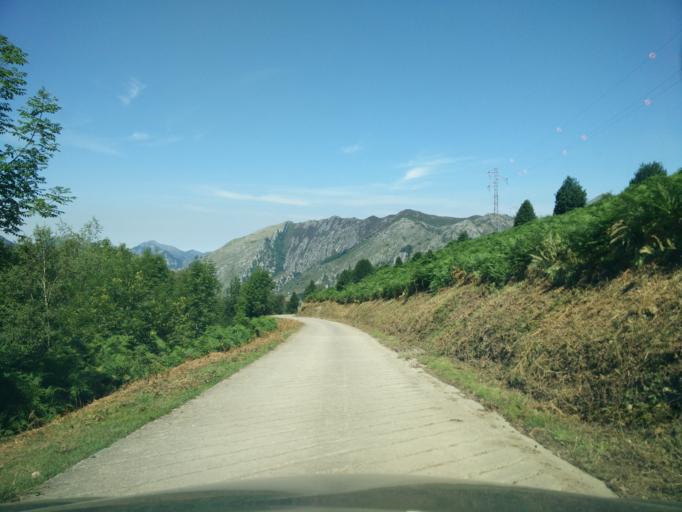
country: ES
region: Asturias
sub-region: Province of Asturias
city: Amieva
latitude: 43.1868
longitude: -5.1422
